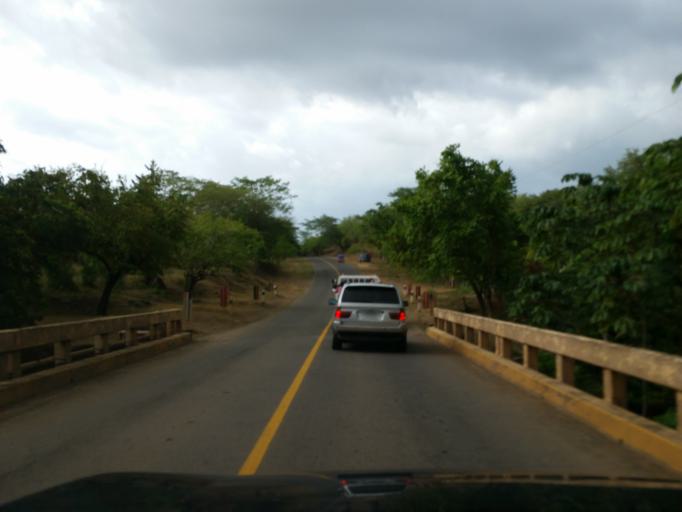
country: NI
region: Managua
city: Carlos Fonseca Amador
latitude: 11.9875
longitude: -86.5150
